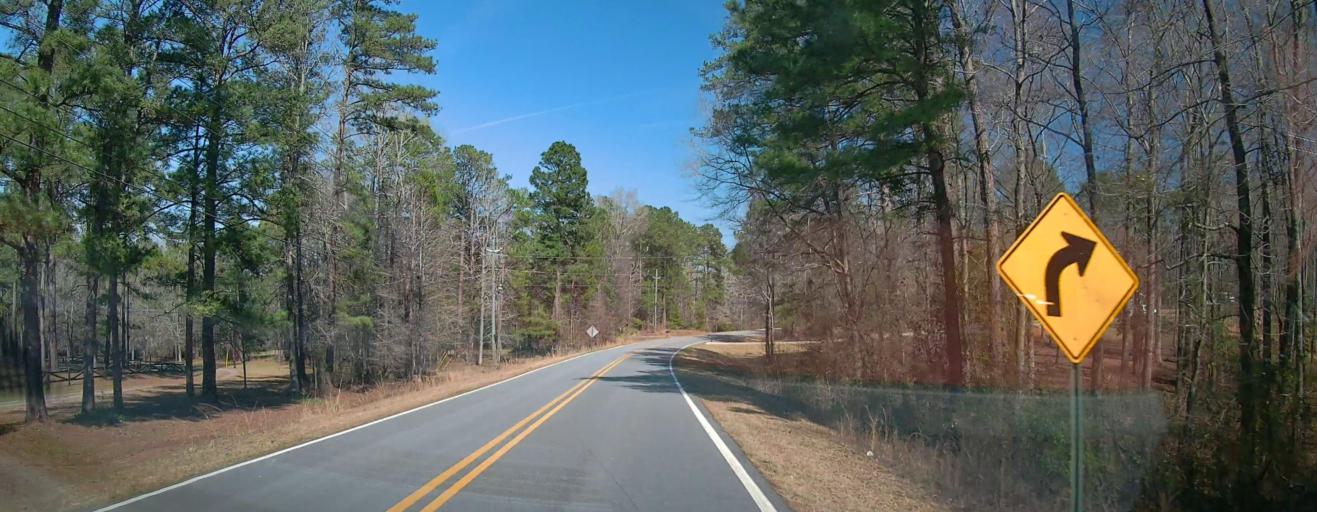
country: US
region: Georgia
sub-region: Bibb County
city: Macon
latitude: 32.9044
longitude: -83.6295
